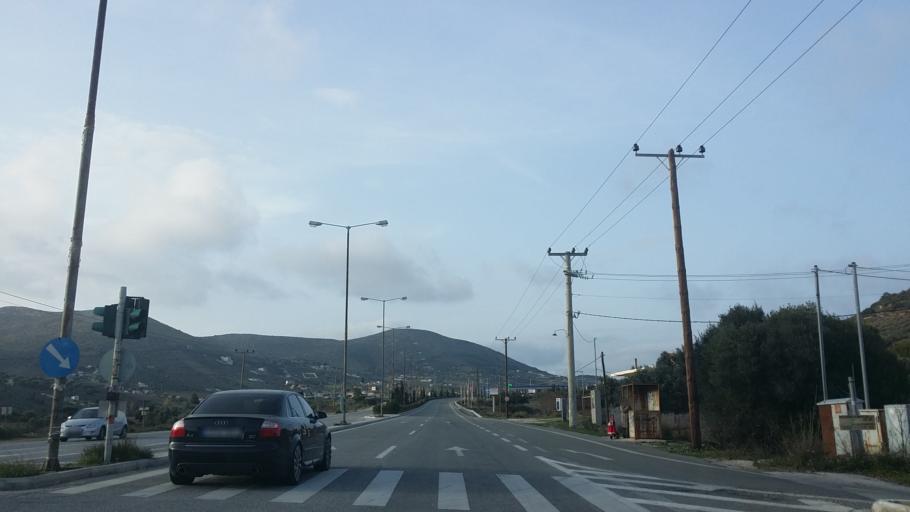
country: GR
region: Attica
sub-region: Nomarchia Anatolikis Attikis
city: Lavrio
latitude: 37.7680
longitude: 24.0557
